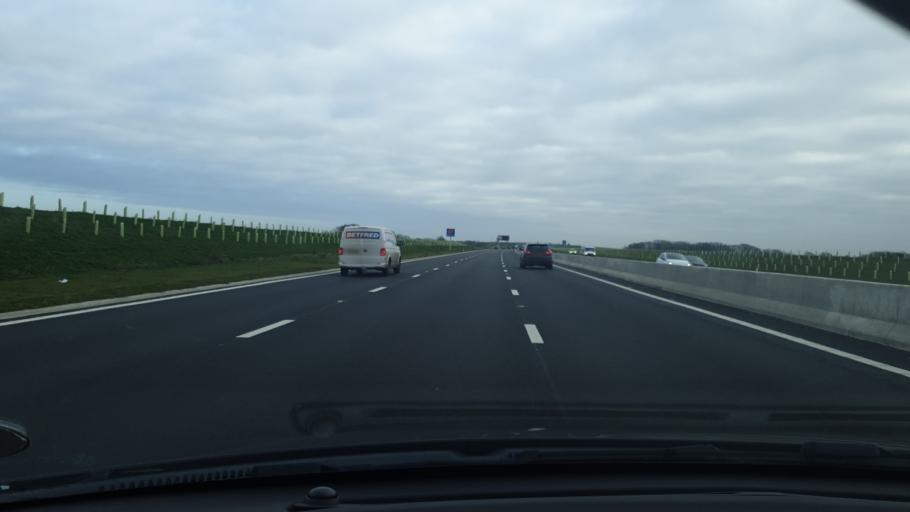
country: GB
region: England
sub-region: Cambridgeshire
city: Hemingford Grey
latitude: 52.2928
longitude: -0.1168
